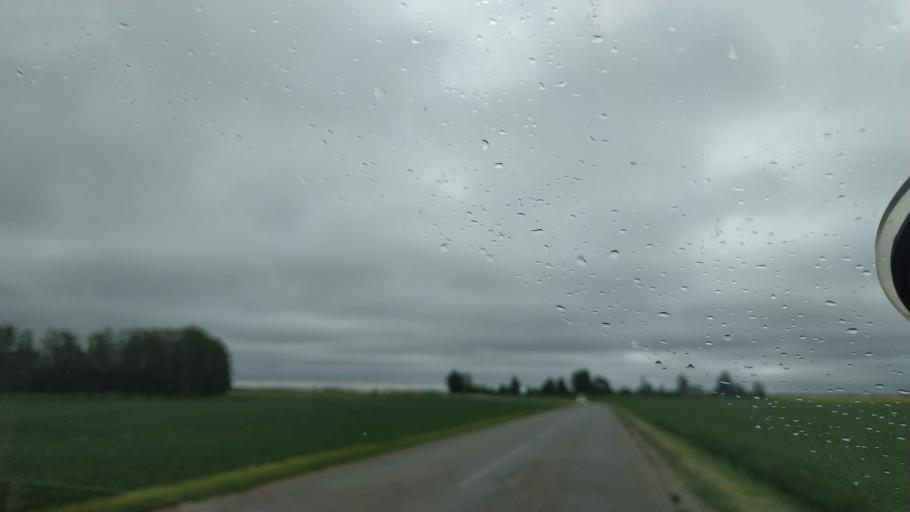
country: LT
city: Vabalninkas
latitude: 55.9924
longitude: 24.6911
